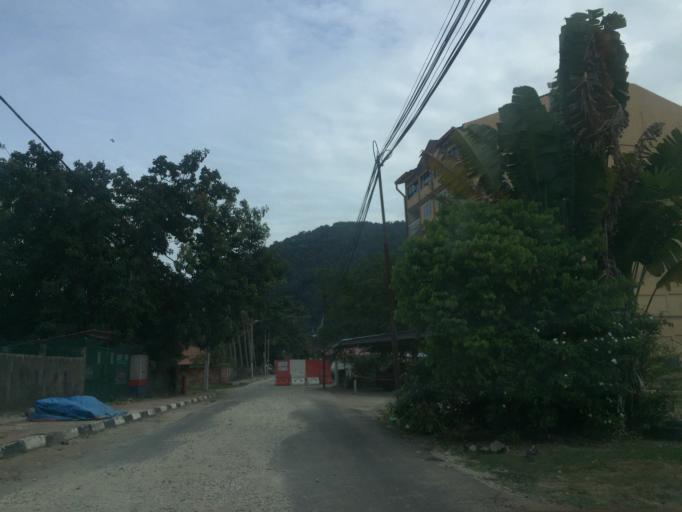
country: MY
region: Perak
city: Lumut
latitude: 4.2088
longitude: 100.5596
